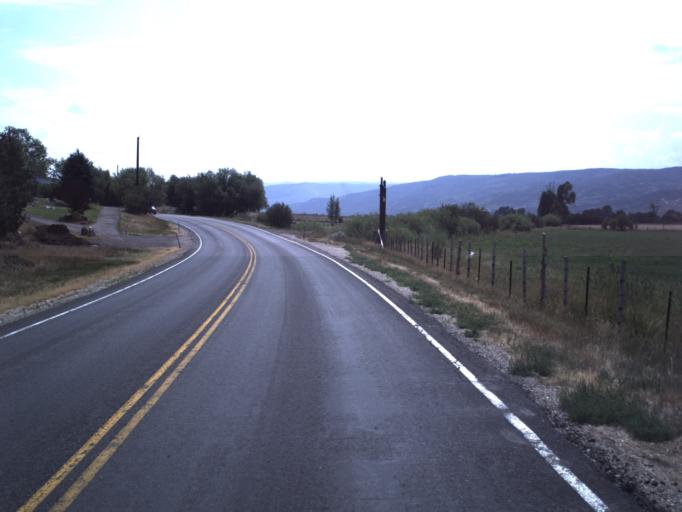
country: US
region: Utah
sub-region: Summit County
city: Francis
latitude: 40.6054
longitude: -111.2548
